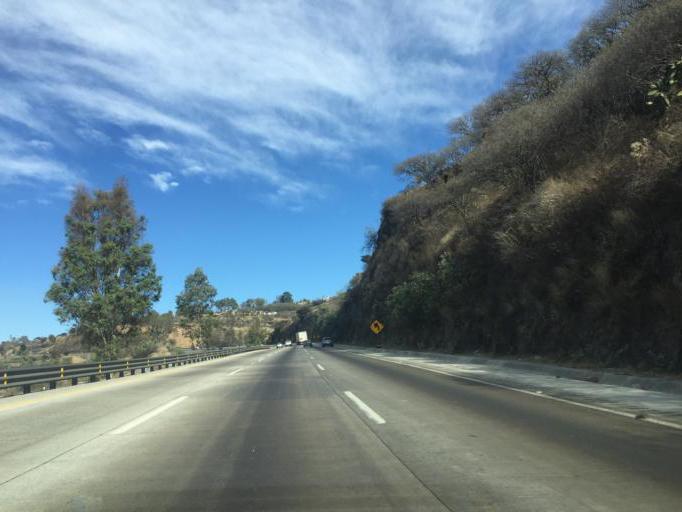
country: MX
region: Hidalgo
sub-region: Tepeji del Rio de Ocampo
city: Santiago Tlautla
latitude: 19.9664
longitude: -99.4273
